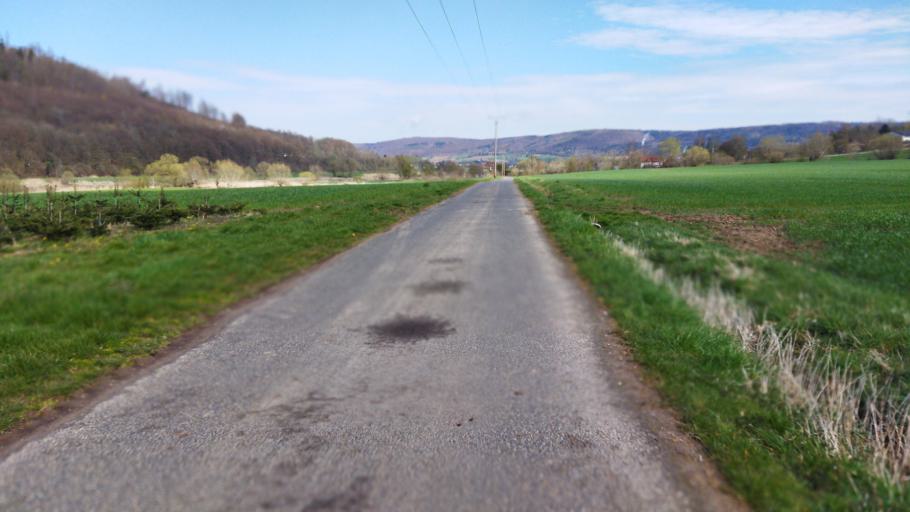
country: DE
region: Lower Saxony
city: Bodenfelde
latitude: 51.6134
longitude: 9.5459
